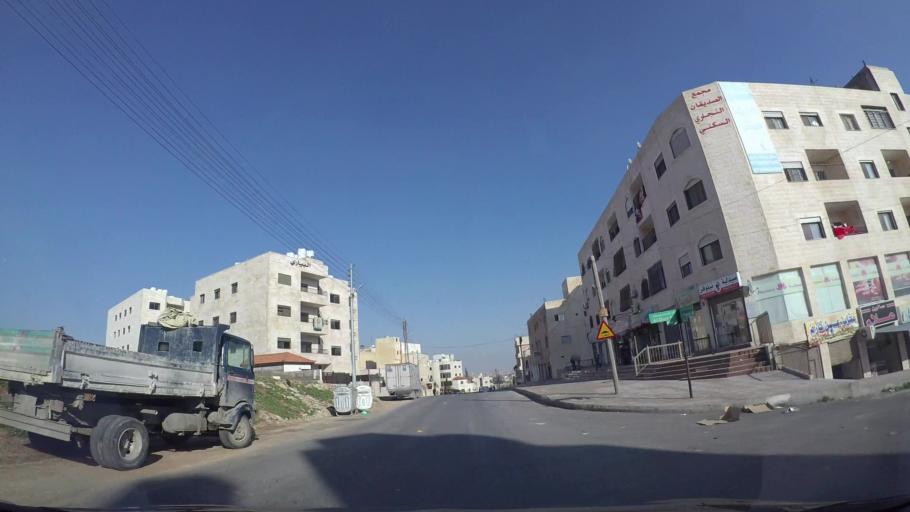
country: JO
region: Amman
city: Amman
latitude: 31.9774
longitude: 35.9624
